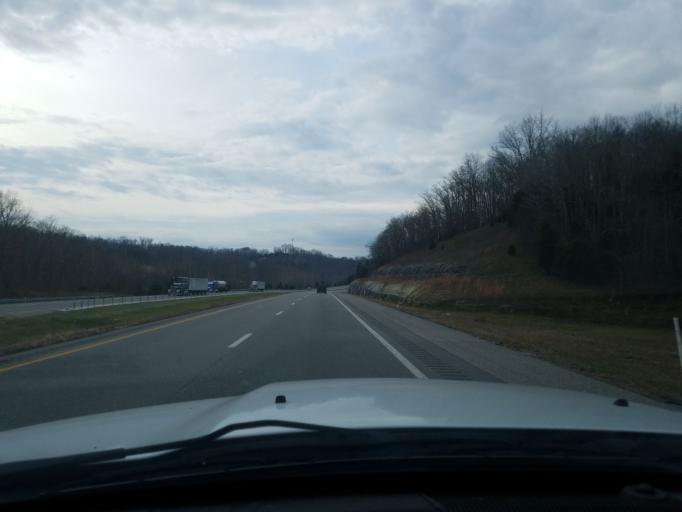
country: US
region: Kentucky
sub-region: Carter County
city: Olive Hill
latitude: 38.3226
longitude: -83.1636
